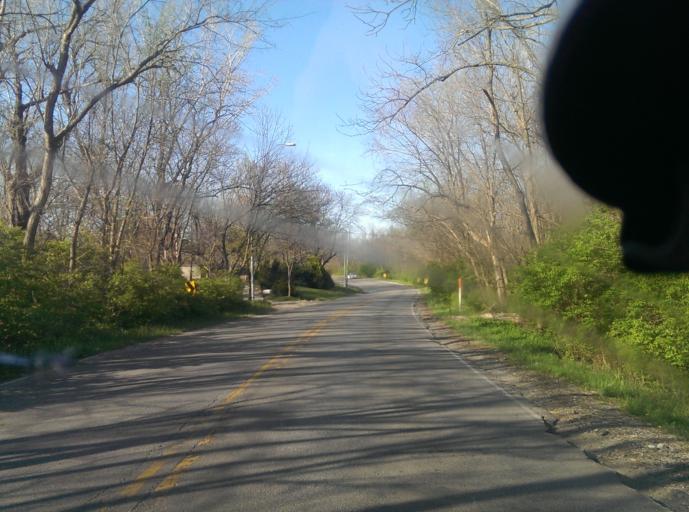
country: US
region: Missouri
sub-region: Jackson County
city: Grandview
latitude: 38.8949
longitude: -94.5863
